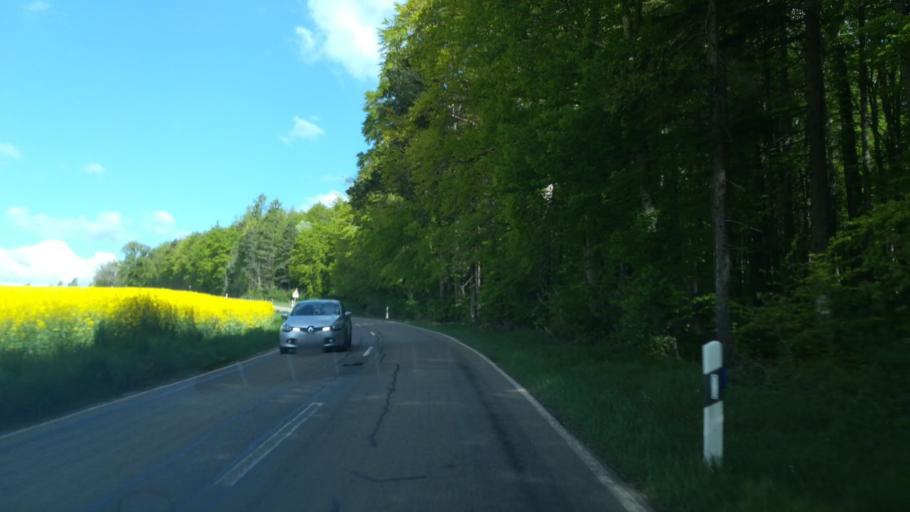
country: DE
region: Baden-Wuerttemberg
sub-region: Freiburg Region
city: Stuhlingen
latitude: 47.7495
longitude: 8.4172
